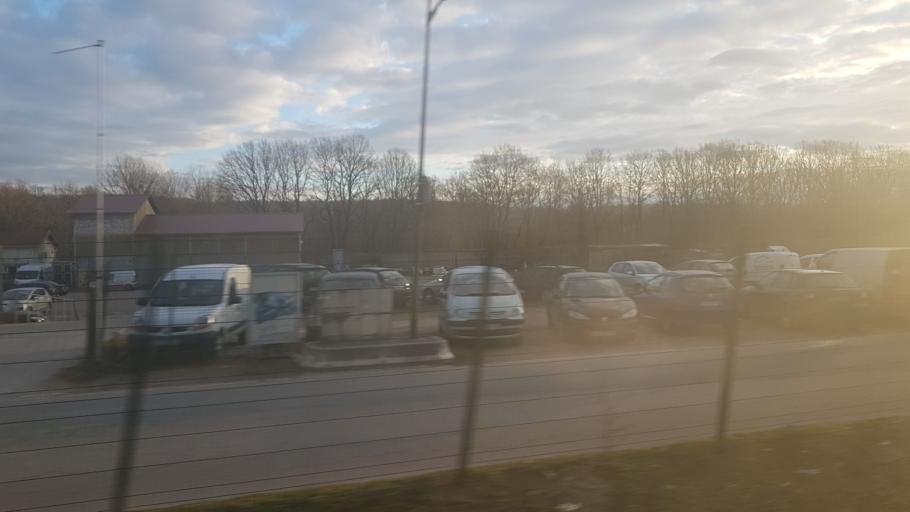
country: FR
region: Lorraine
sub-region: Departement des Vosges
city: Nomexy
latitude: 48.3032
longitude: 6.3911
